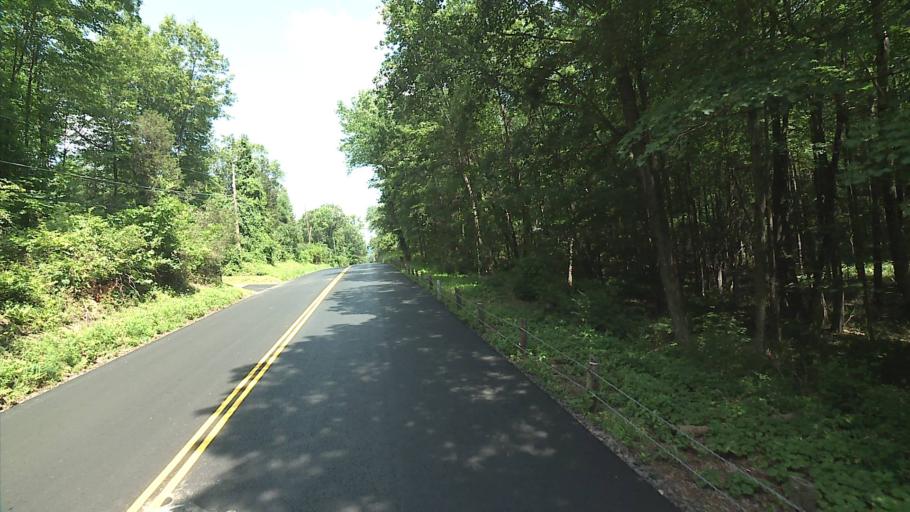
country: US
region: Connecticut
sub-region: Litchfield County
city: Canaan
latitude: 41.9853
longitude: -73.3612
